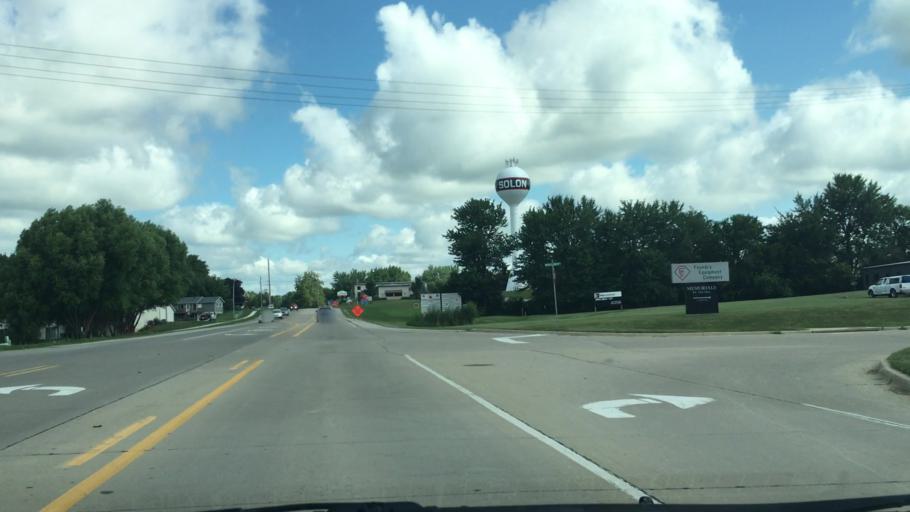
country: US
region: Iowa
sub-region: Johnson County
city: Solon
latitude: 41.7989
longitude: -91.4909
